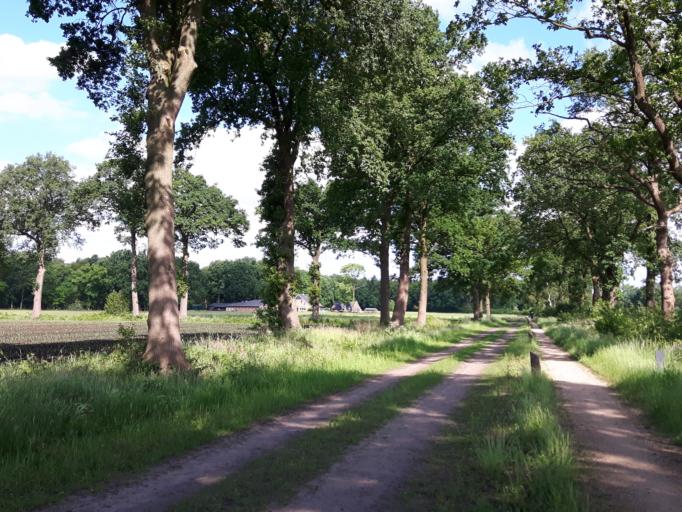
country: NL
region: Overijssel
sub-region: Gemeente Enschede
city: Enschede
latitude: 52.1673
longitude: 6.8319
